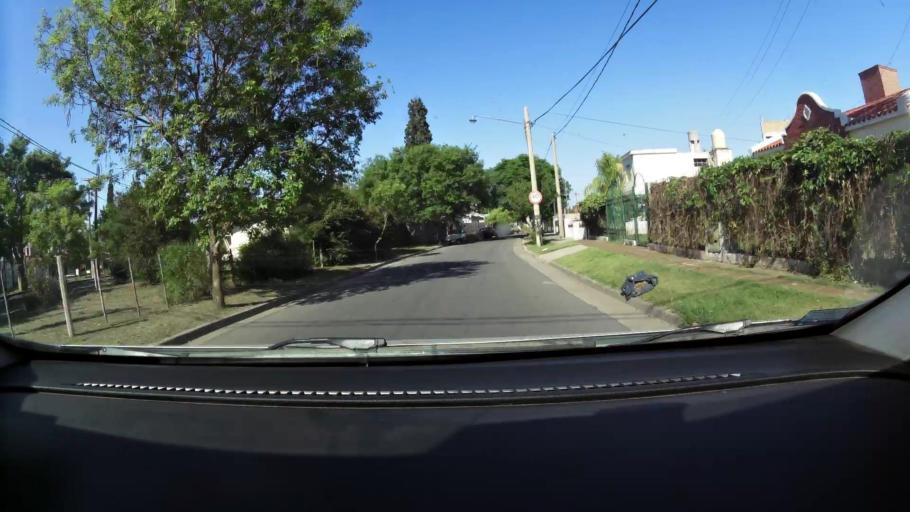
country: AR
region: Cordoba
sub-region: Departamento de Capital
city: Cordoba
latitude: -31.3618
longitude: -64.1947
